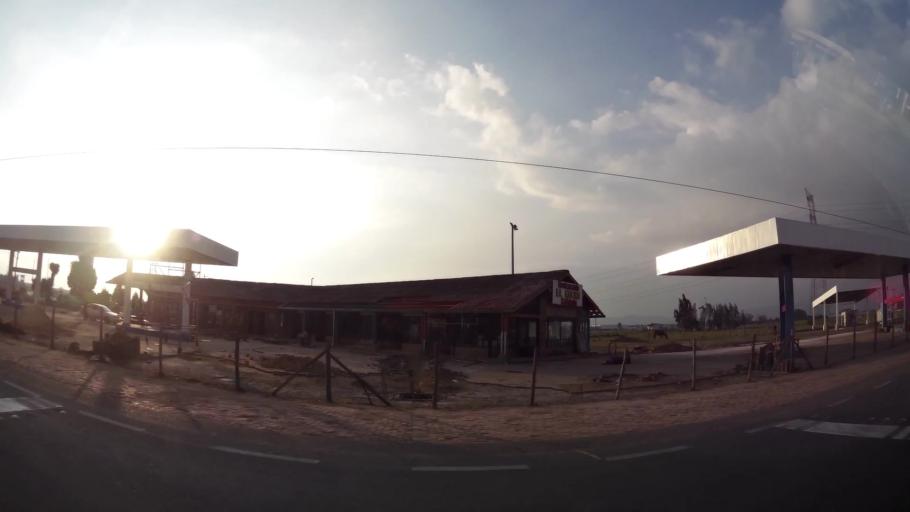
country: CO
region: Cundinamarca
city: Cota
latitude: 4.7639
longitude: -74.1527
